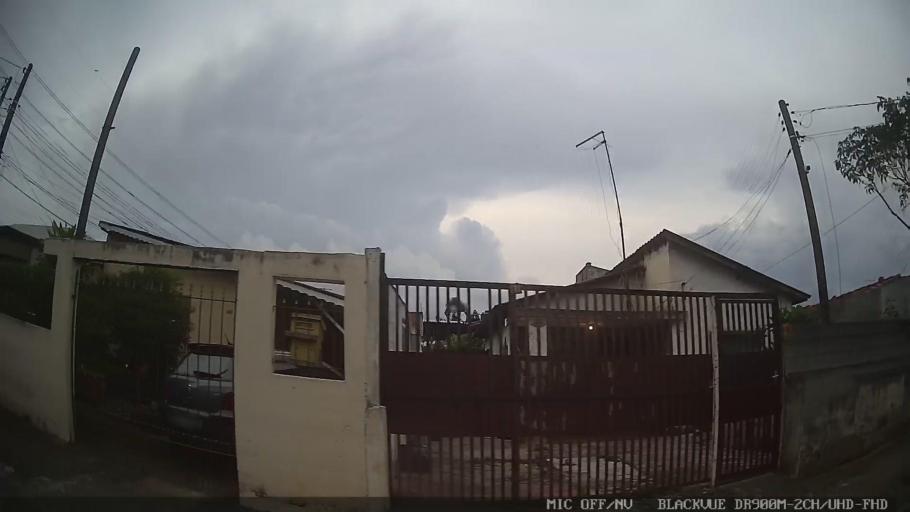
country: BR
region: Sao Paulo
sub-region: Suzano
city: Suzano
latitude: -23.5385
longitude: -46.3026
